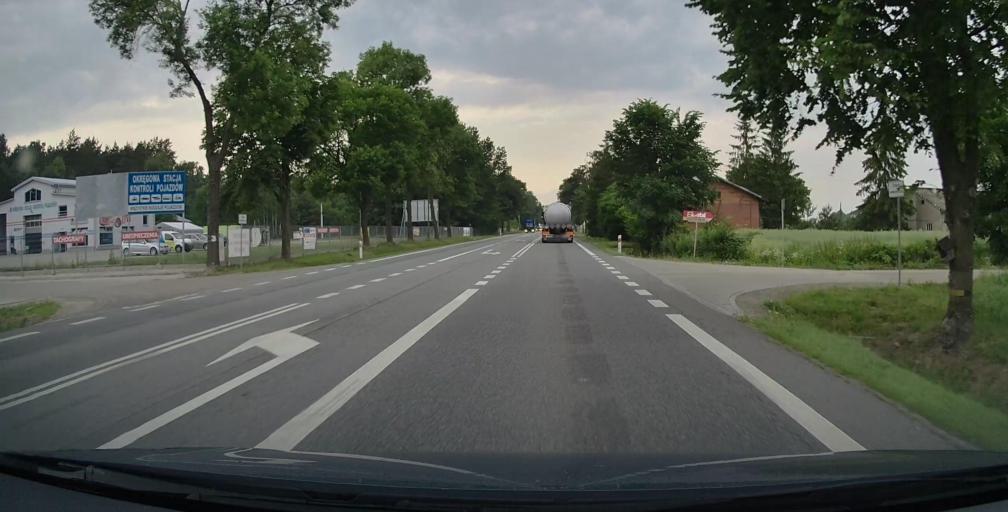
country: PL
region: Masovian Voivodeship
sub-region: Powiat siedlecki
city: Zbuczyn
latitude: 52.0964
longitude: 22.4149
